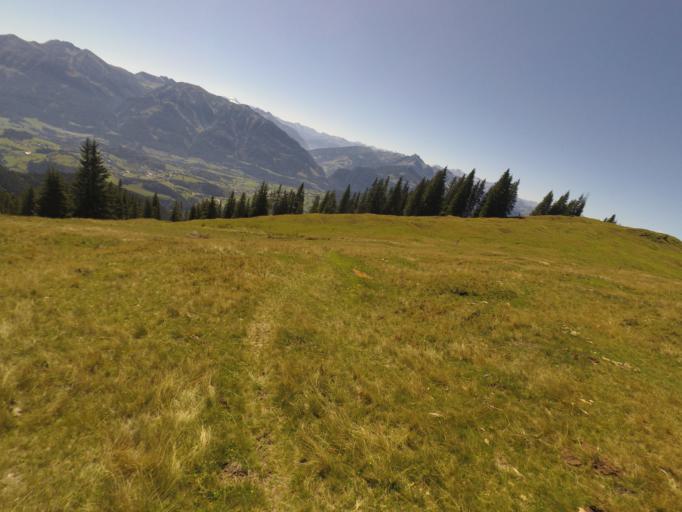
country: AT
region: Salzburg
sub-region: Politischer Bezirk Sankt Johann im Pongau
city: Goldegg
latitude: 47.3500
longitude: 13.0693
